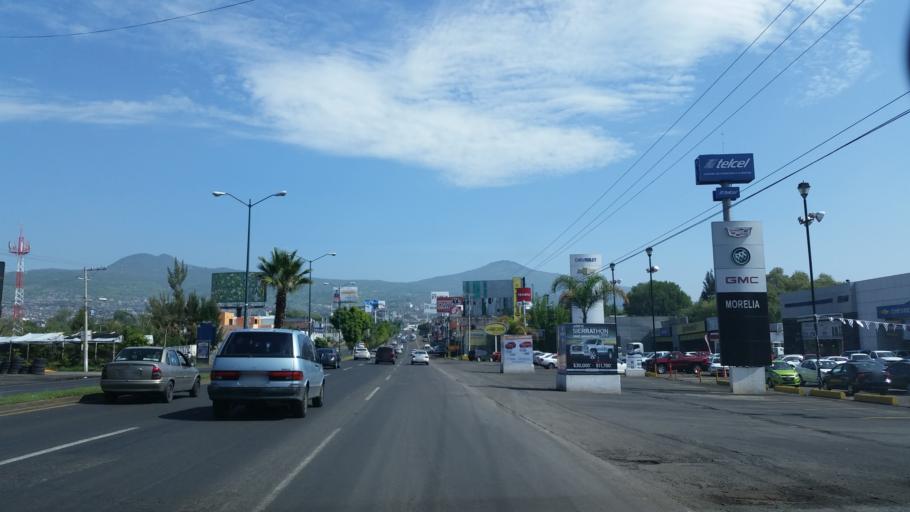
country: MX
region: Michoacan
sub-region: Morelia
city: San Antonio
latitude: 19.6905
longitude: -101.2393
